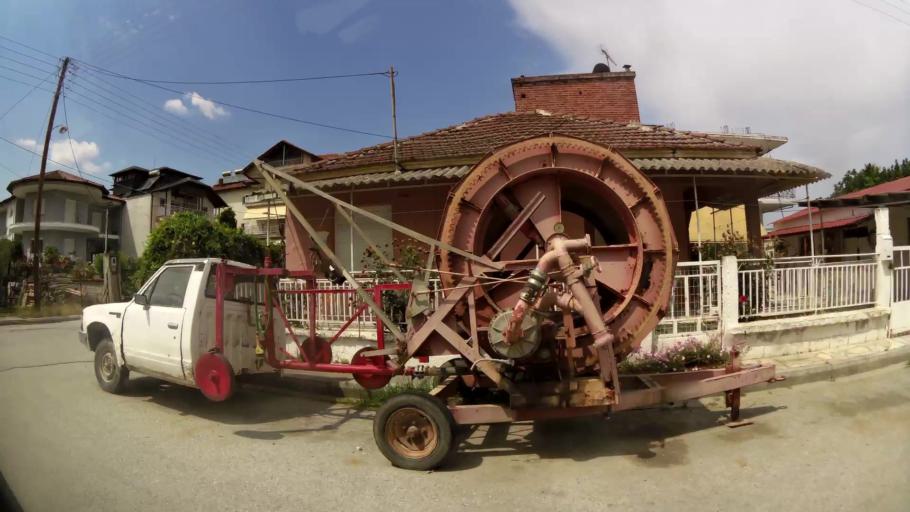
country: GR
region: Central Macedonia
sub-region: Nomos Pierias
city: Korinos
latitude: 40.3123
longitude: 22.5783
